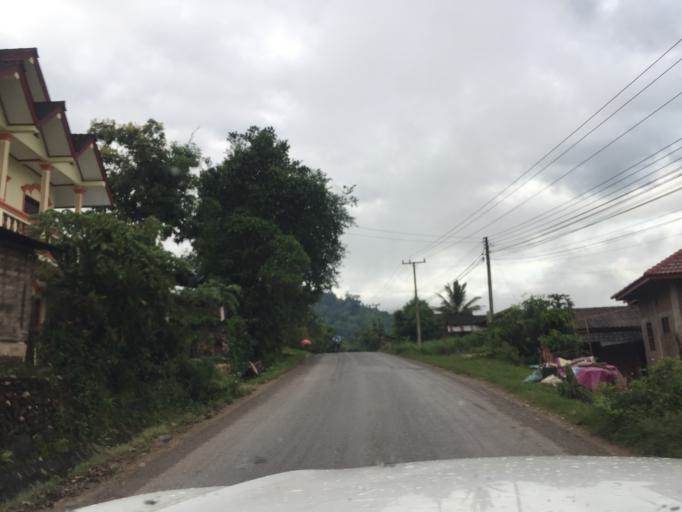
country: LA
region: Oudomxai
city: Muang La
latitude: 20.8668
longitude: 102.1165
